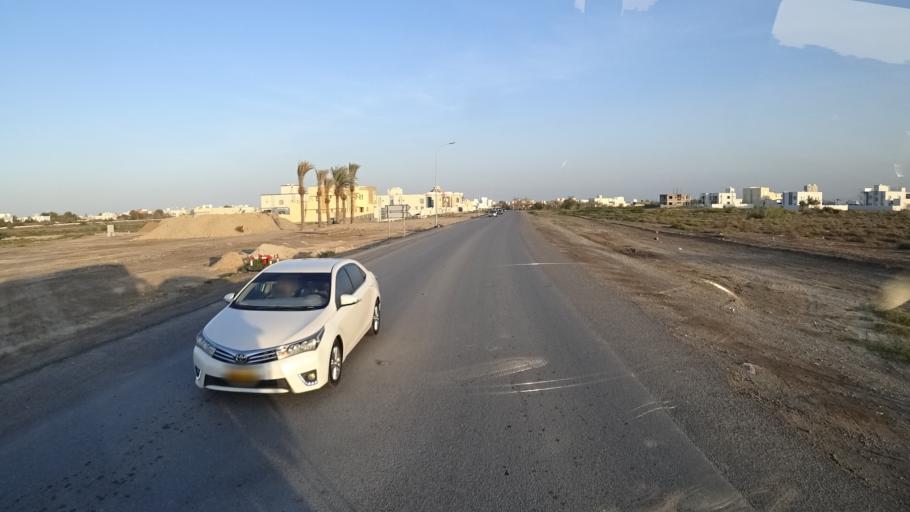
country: OM
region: Al Batinah
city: Barka'
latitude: 23.7030
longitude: 57.9187
